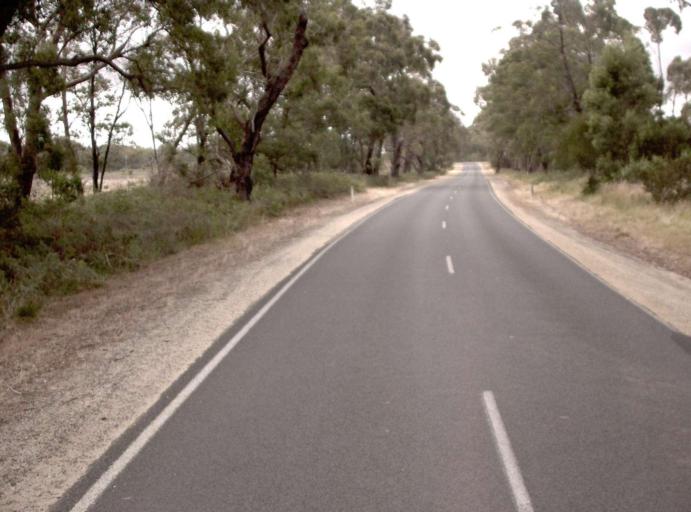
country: AU
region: Victoria
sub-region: Wellington
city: Sale
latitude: -38.2202
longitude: 147.1091
